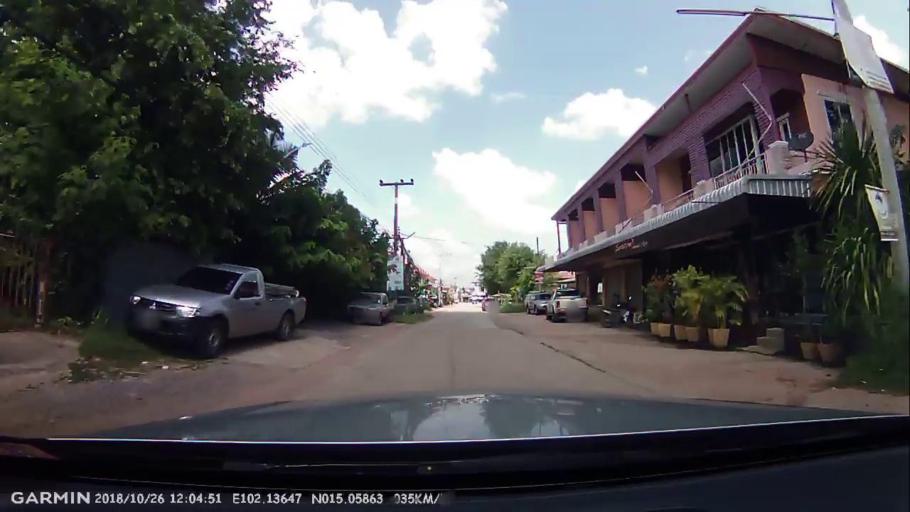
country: TH
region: Nakhon Ratchasima
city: Nakhon Ratchasima
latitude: 15.0585
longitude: 102.1365
